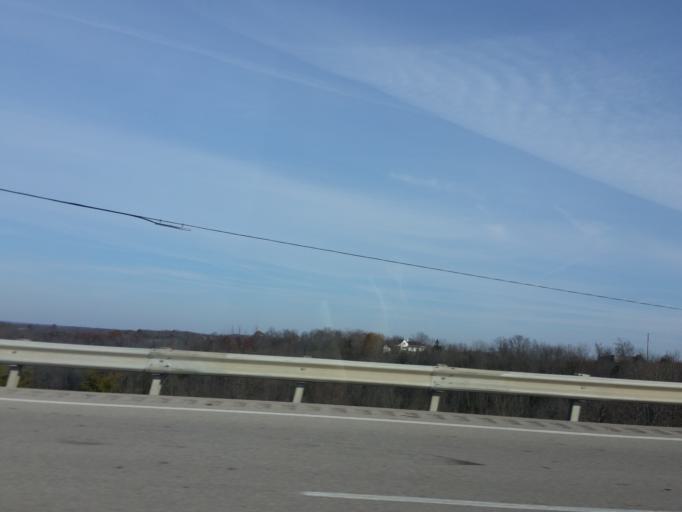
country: US
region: Kentucky
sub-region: Pendleton County
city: Falmouth
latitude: 38.5499
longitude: -84.2887
